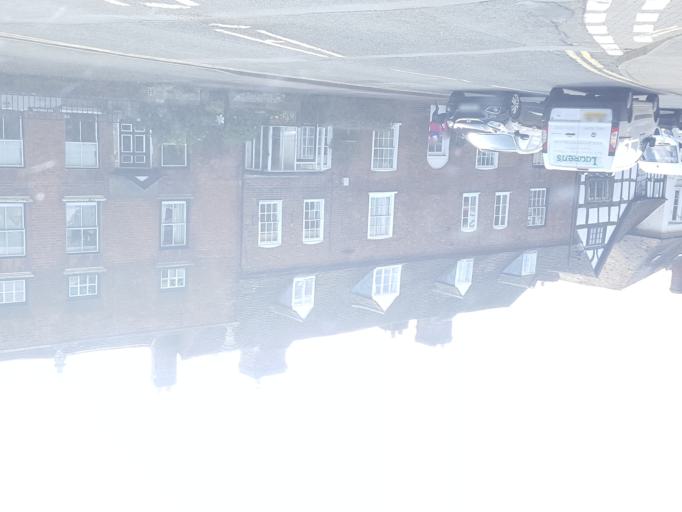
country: GB
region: England
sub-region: Worcestershire
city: Upton upon Severn
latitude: 52.0646
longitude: -2.2183
